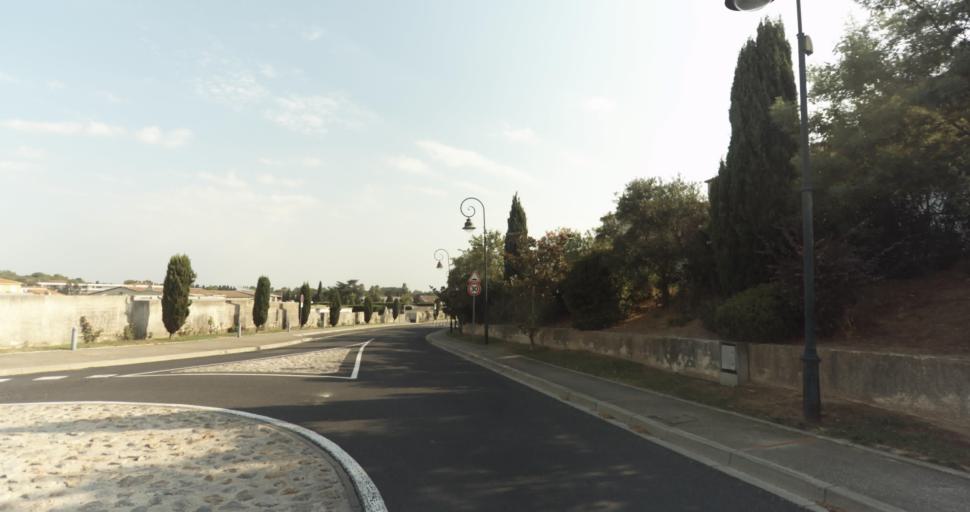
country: FR
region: Languedoc-Roussillon
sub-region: Departement des Pyrenees-Orientales
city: Latour-Bas-Elne
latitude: 42.6150
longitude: 2.9974
